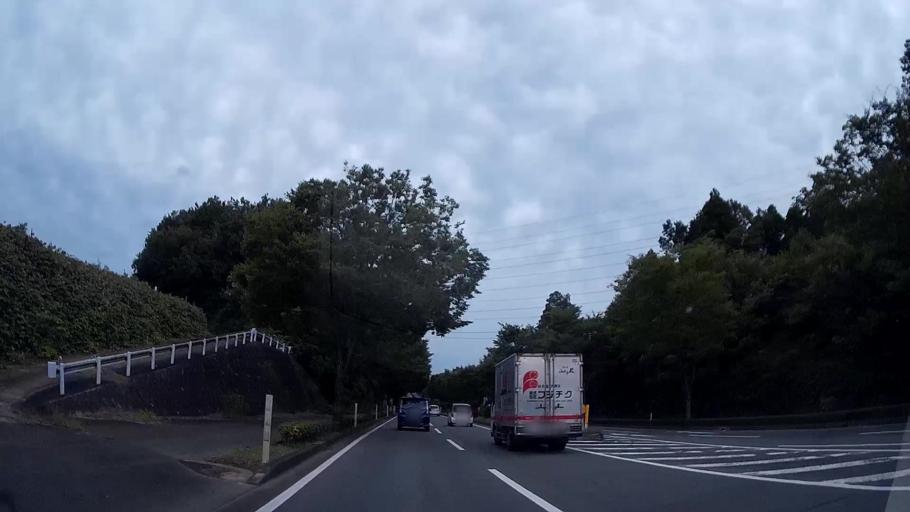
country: JP
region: Kumamoto
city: Ozu
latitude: 32.9169
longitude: 130.8392
